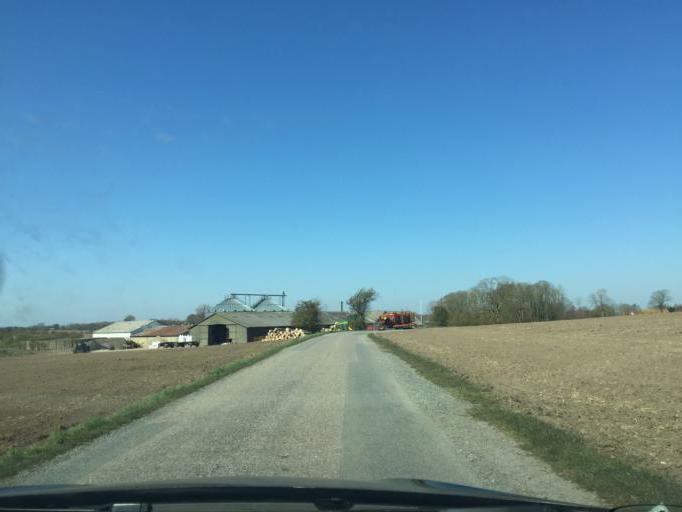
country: DK
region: South Denmark
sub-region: Faaborg-Midtfyn Kommune
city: Arslev
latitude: 55.2923
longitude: 10.5223
